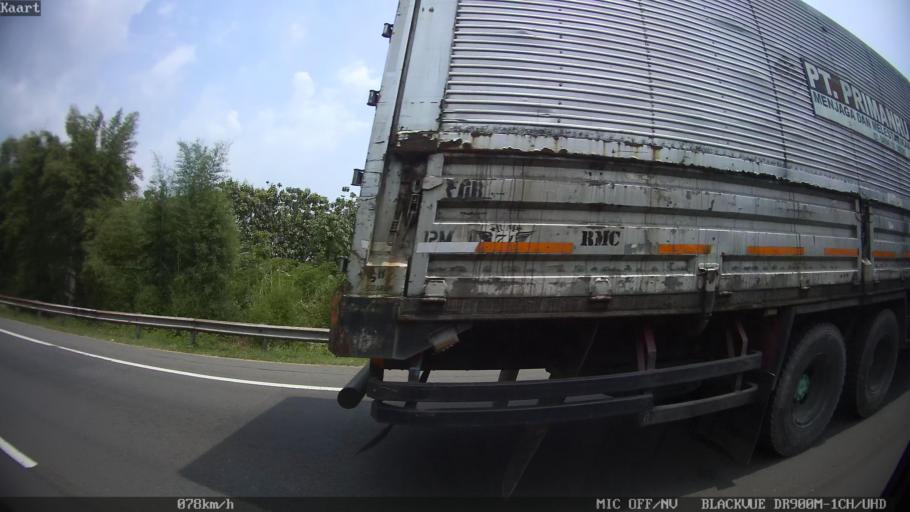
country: ID
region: Banten
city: Curug
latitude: -5.9903
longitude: 106.0439
